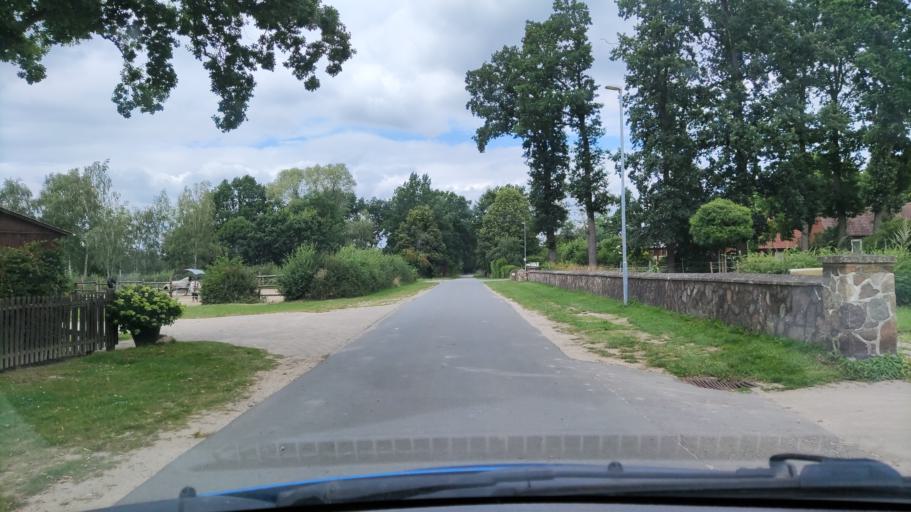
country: DE
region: Lower Saxony
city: Romstedt
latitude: 53.1050
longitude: 10.6787
